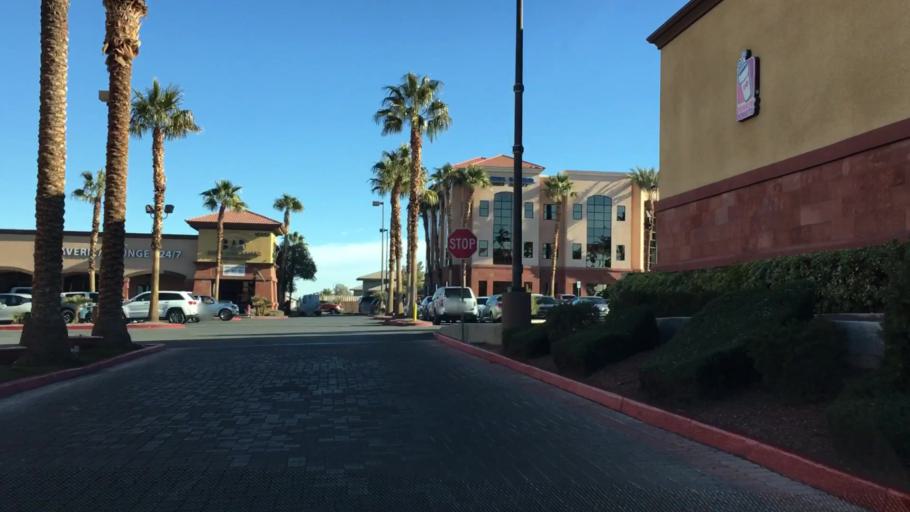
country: US
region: Nevada
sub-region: Clark County
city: Whitney
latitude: 36.0059
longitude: -115.1121
